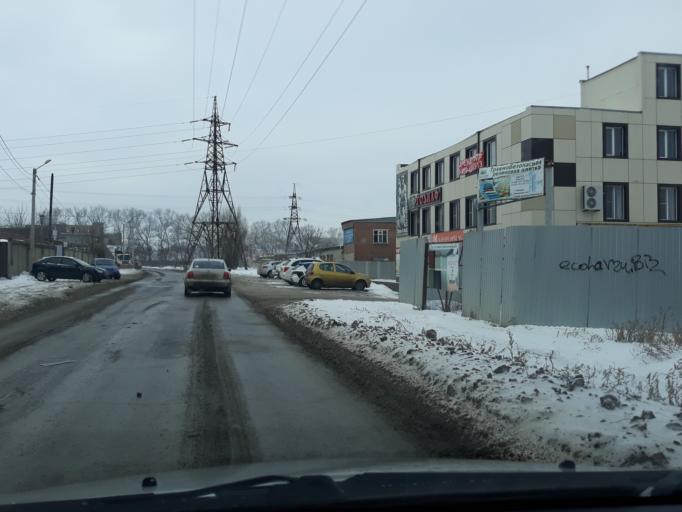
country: RU
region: Rostov
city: Taganrog
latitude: 47.2479
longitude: 38.8885
